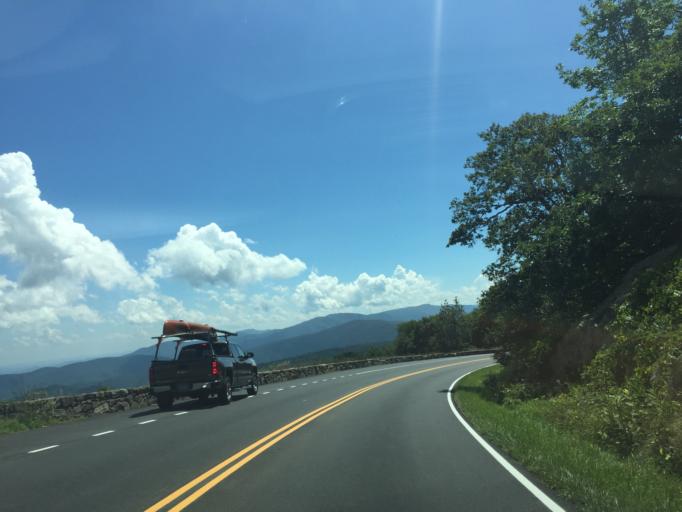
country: US
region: Virginia
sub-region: Rappahannock County
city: Washington
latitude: 38.7522
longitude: -78.2884
